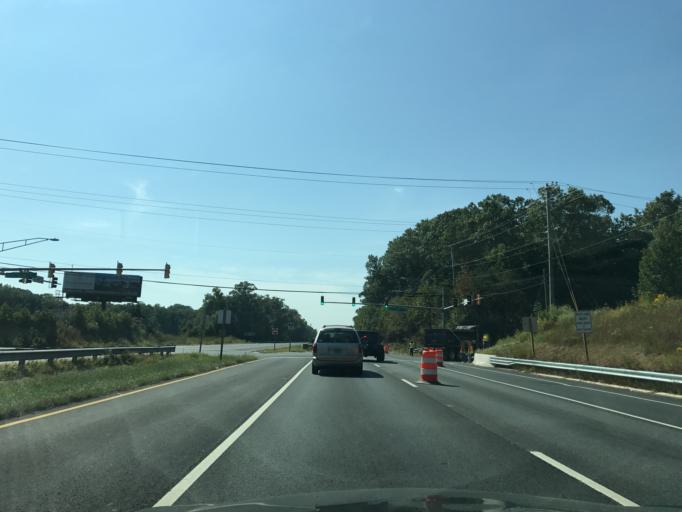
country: US
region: Maryland
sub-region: Cecil County
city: North East
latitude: 39.6029
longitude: -75.9633
